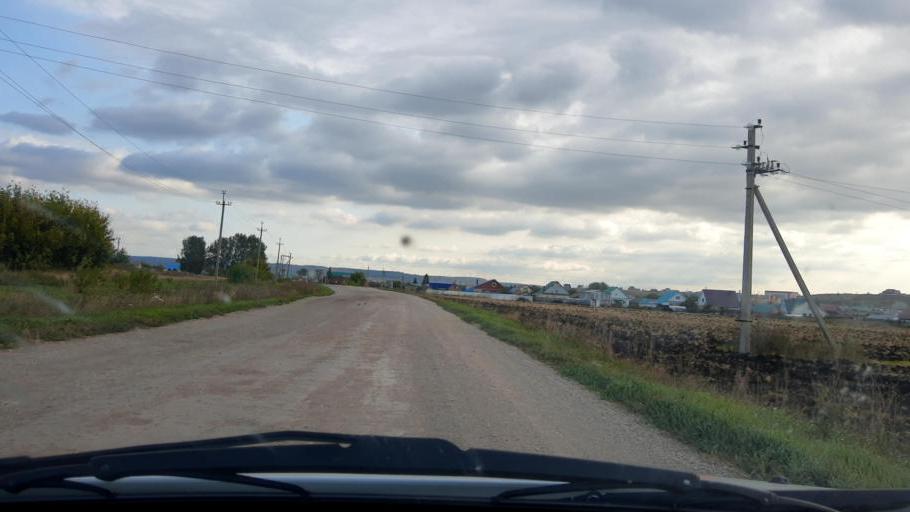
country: RU
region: Bashkortostan
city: Subkhankulovo
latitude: 54.5432
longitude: 53.7701
